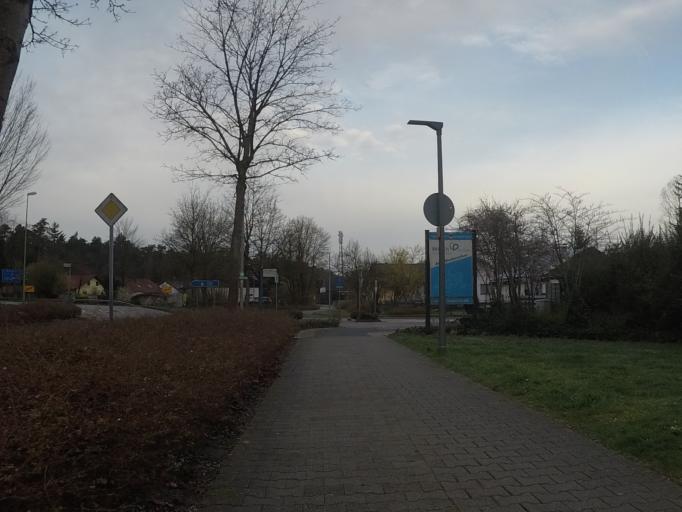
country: DE
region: Rheinland-Pfalz
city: Worth am Rhein
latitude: 49.0521
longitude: 8.2430
